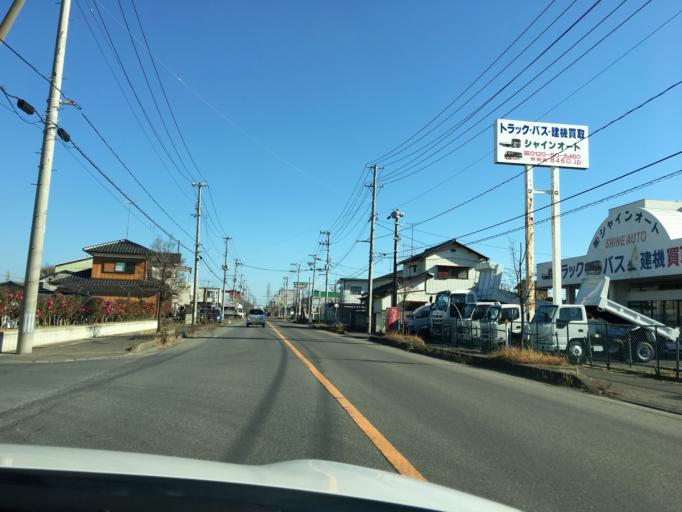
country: JP
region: Fukushima
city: Iwaki
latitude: 36.9384
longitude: 140.8593
